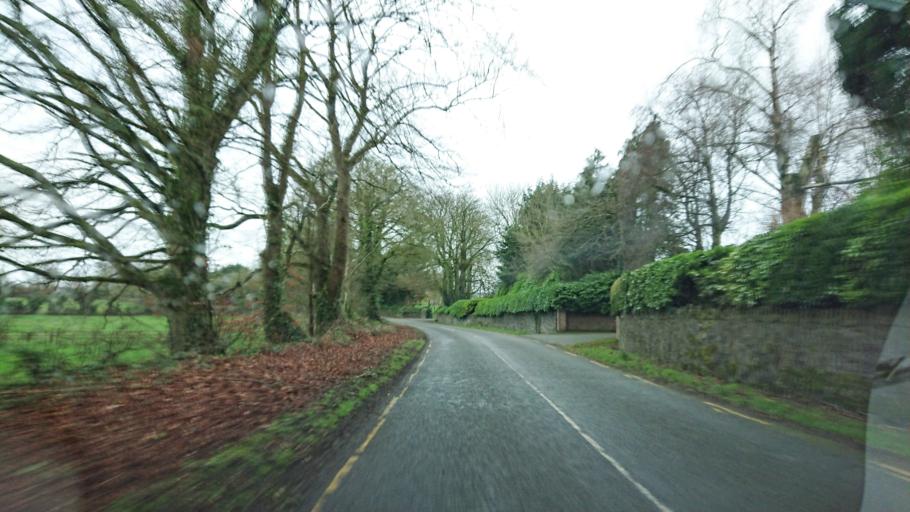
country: IE
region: Leinster
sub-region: Kilkenny
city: Callan
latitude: 52.5370
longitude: -7.2910
